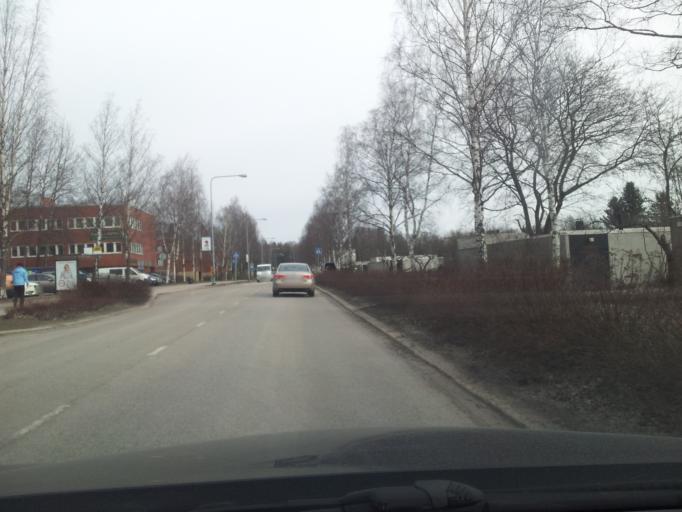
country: FI
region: Uusimaa
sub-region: Helsinki
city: Otaniemi
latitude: 60.1838
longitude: 24.7951
